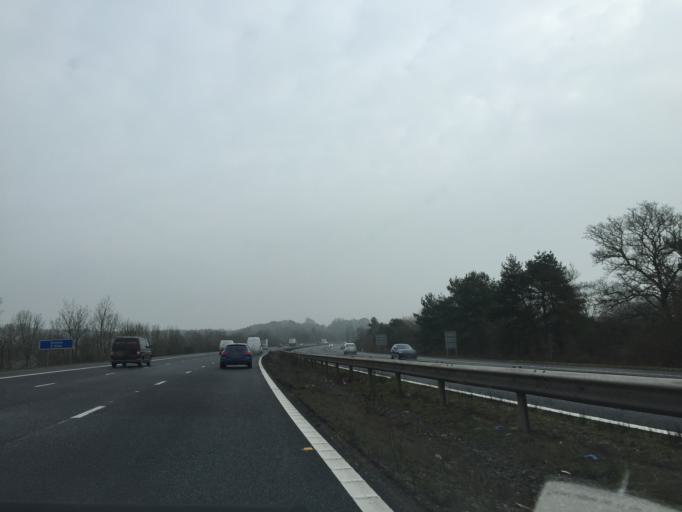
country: GB
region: England
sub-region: Hampshire
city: Cadnam
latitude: 50.9269
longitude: -1.5771
